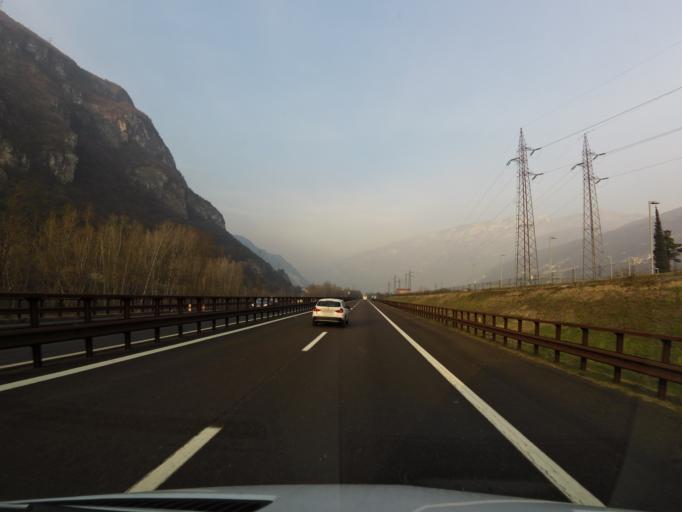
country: IT
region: Trentino-Alto Adige
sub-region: Provincia di Trento
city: Ala
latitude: 45.7594
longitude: 10.9953
